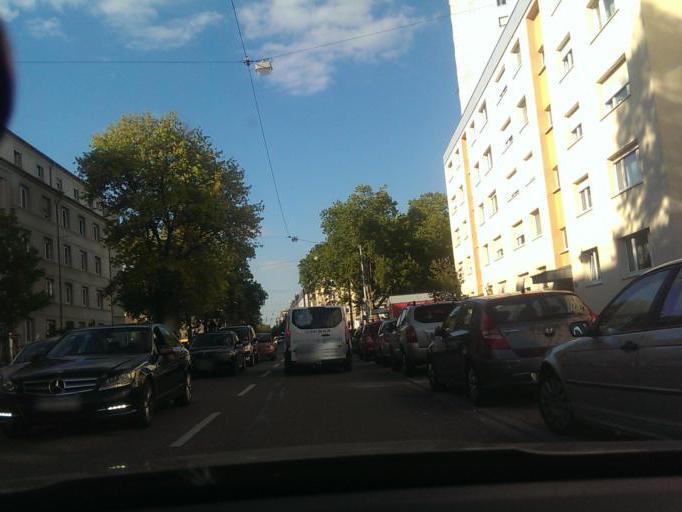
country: DE
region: Baden-Wuerttemberg
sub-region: Karlsruhe Region
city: Karlsruhe
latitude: 49.0063
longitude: 8.4243
